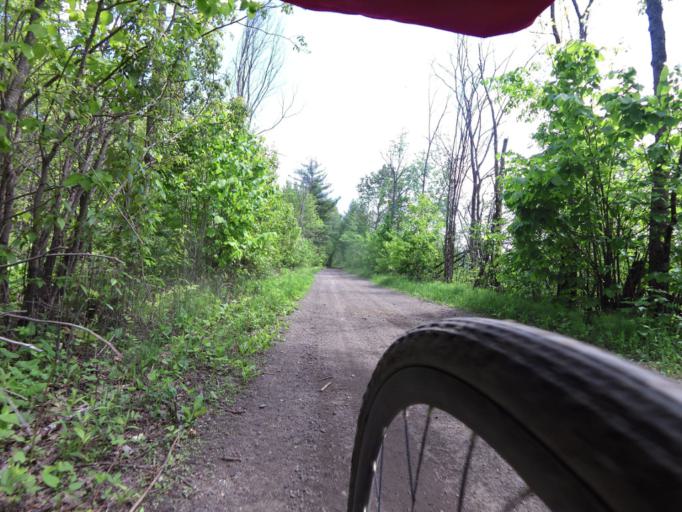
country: CA
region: Ontario
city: Renfrew
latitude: 45.2030
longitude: -76.6867
